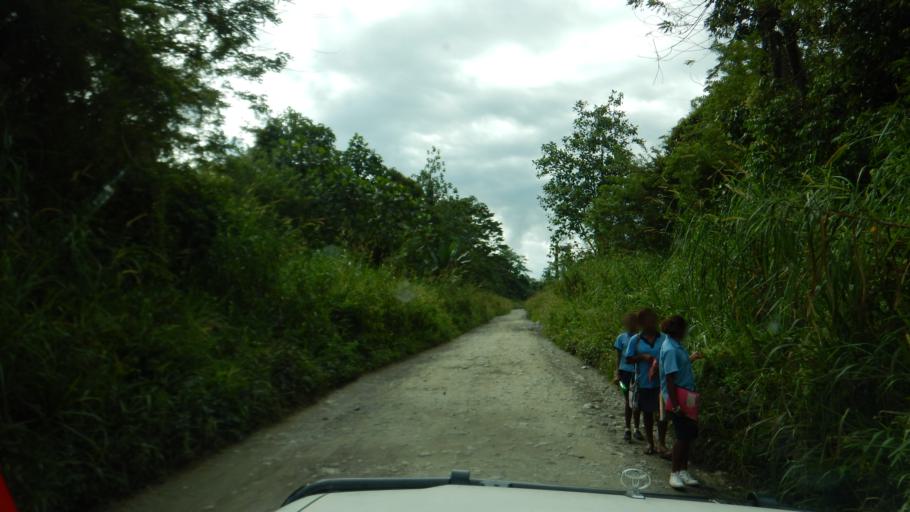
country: PG
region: Northern Province
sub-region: Sohe
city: Kokoda
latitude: -8.8887
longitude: 147.7468
